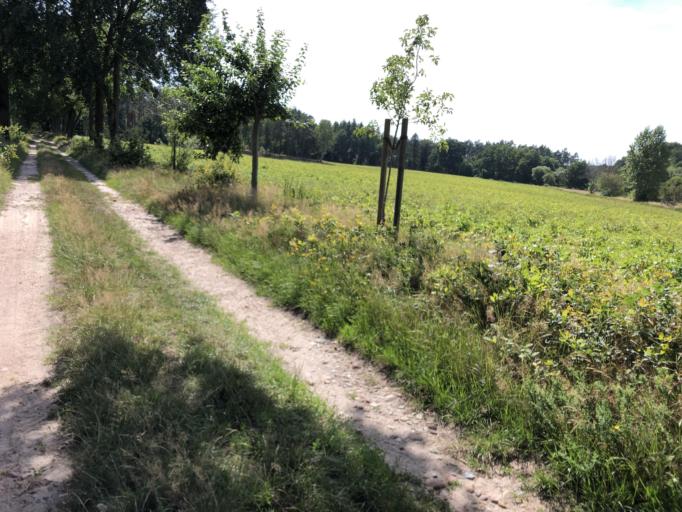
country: DE
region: Lower Saxony
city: Thomasburg
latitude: 53.2069
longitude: 10.6985
